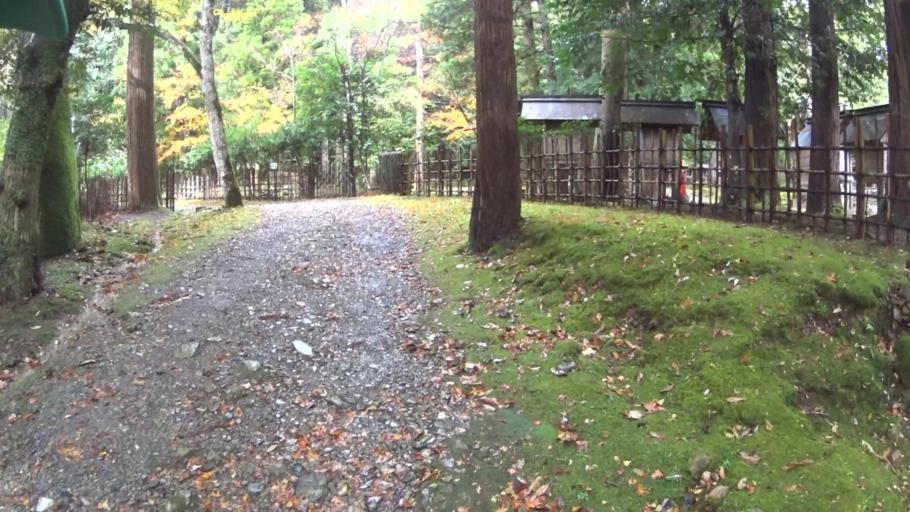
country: JP
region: Kyoto
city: Miyazu
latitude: 35.4301
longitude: 135.1538
